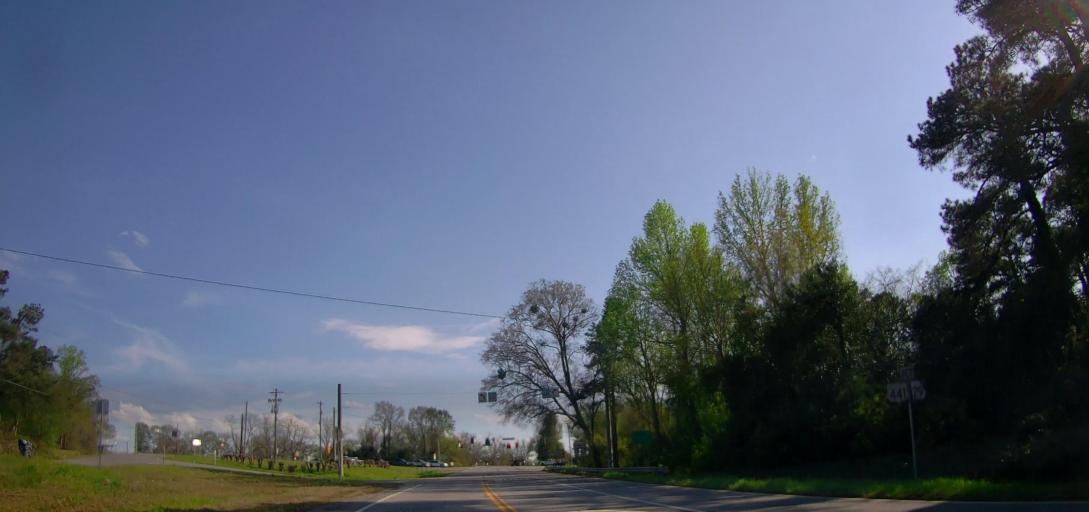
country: US
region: Georgia
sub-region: Baldwin County
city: Hardwick
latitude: 33.0248
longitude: -83.2346
